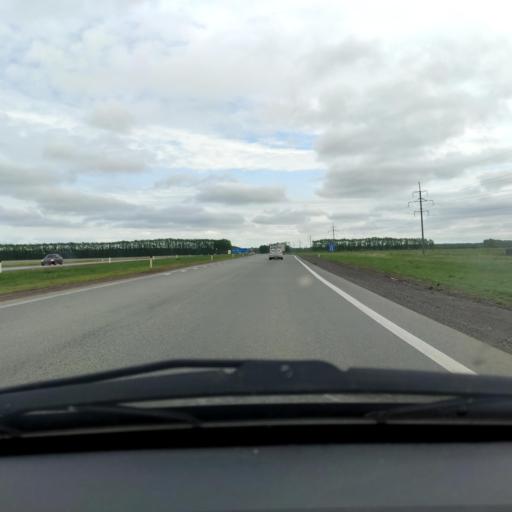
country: RU
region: Bashkortostan
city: Asanovo
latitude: 54.9999
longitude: 55.4977
